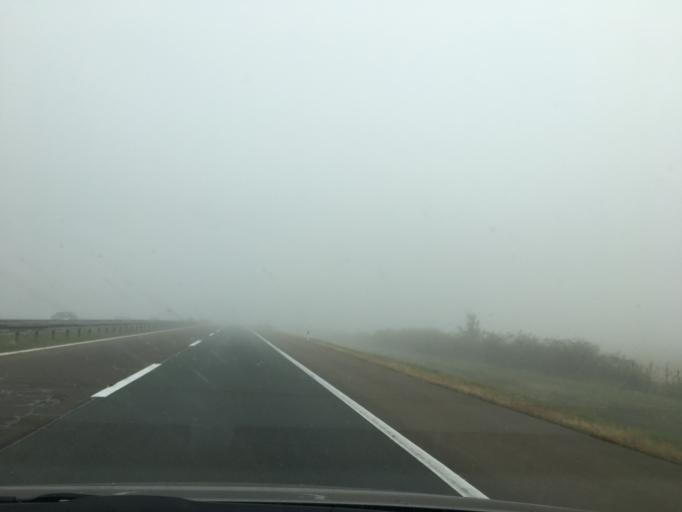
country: RS
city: Novi Karlovci
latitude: 45.0337
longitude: 20.1861
